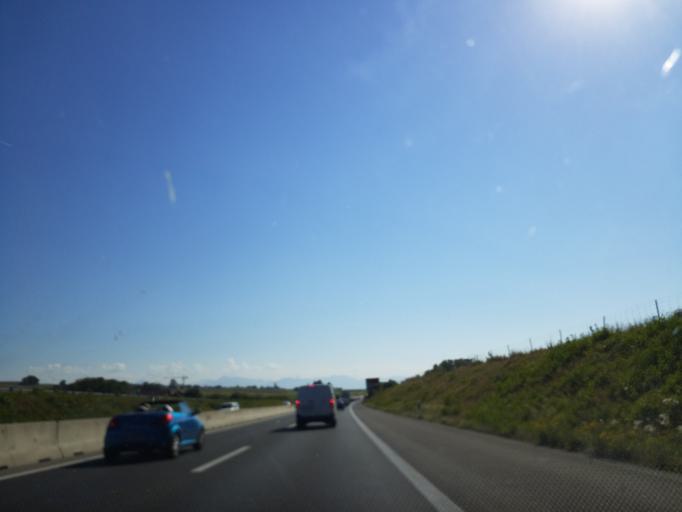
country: CH
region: Vaud
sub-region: Gros-de-Vaud District
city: Penthalaz
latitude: 46.6221
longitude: 6.5601
